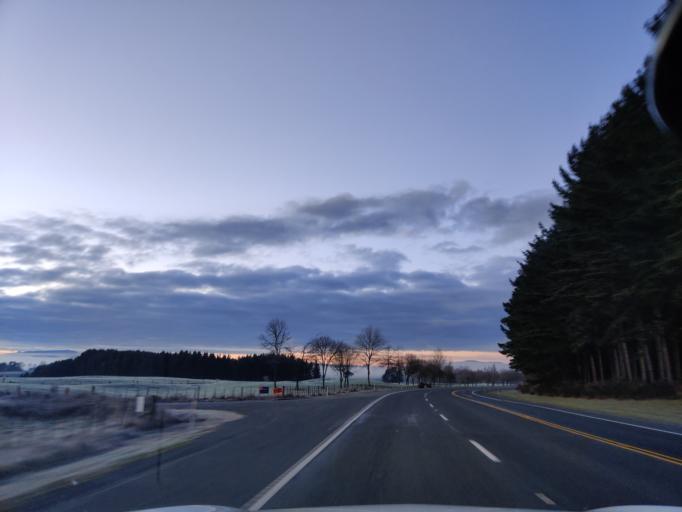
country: NZ
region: Waikato
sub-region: South Waikato District
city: Tokoroa
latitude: -38.3322
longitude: 176.0022
